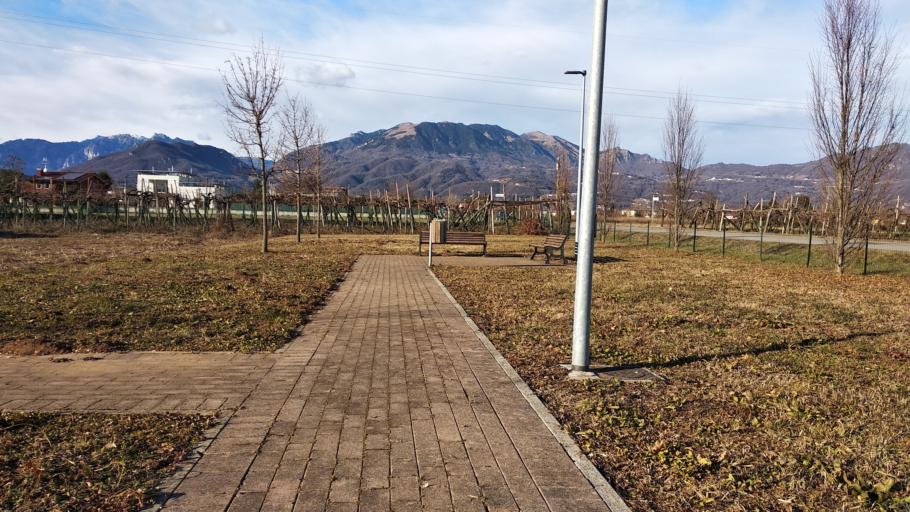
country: IT
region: Veneto
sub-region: Provincia di Vicenza
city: San Vito di Leguzzano
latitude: 45.6912
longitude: 11.3743
